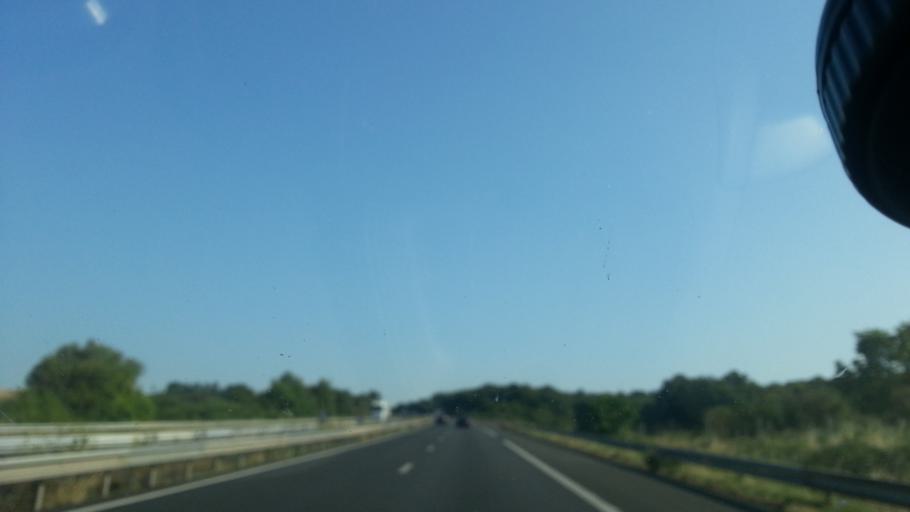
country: FR
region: Poitou-Charentes
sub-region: Departement de la Vienne
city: Dange-Saint-Romain
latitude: 46.9517
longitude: 0.5491
